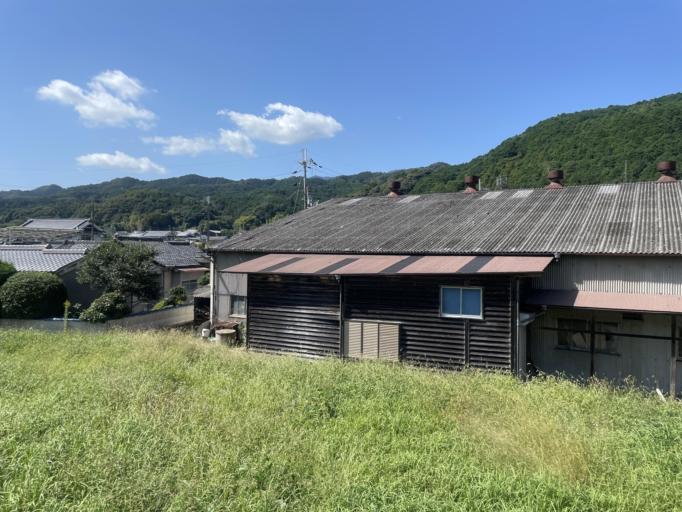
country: JP
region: Nara
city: Gose
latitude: 34.4147
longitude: 135.7483
